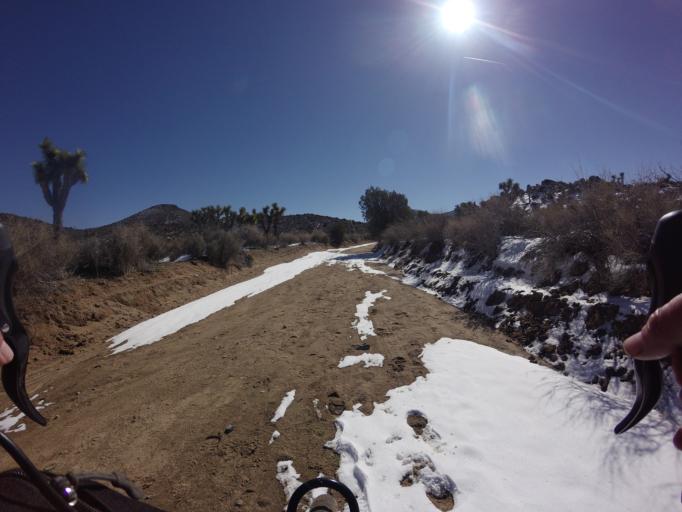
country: US
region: California
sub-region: Riverside County
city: Sky Valley
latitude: 33.9531
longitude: -116.1638
